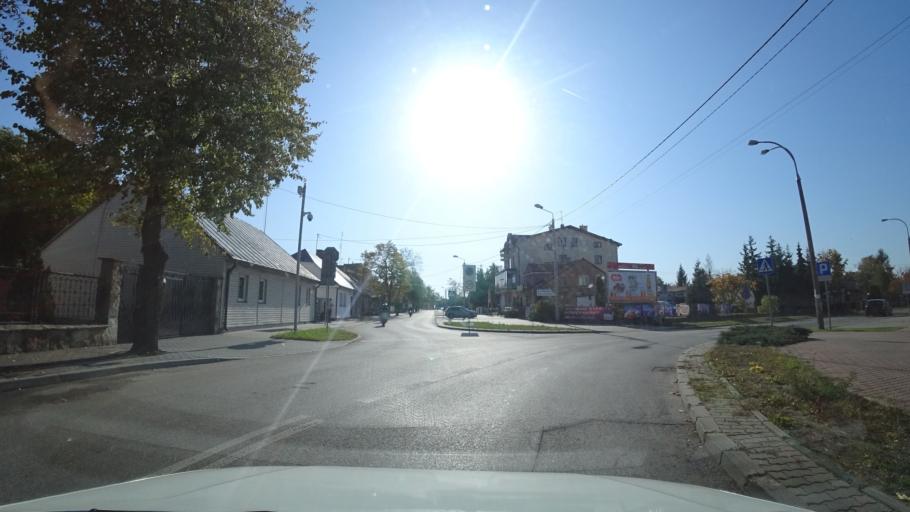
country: PL
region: Masovian Voivodeship
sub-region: Powiat wegrowski
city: Wegrow
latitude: 52.4016
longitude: 22.0156
